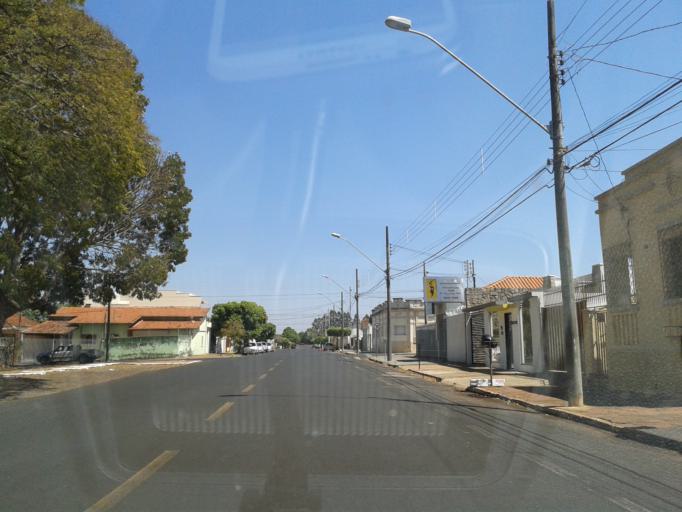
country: BR
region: Minas Gerais
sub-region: Araguari
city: Araguari
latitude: -18.6420
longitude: -48.1920
